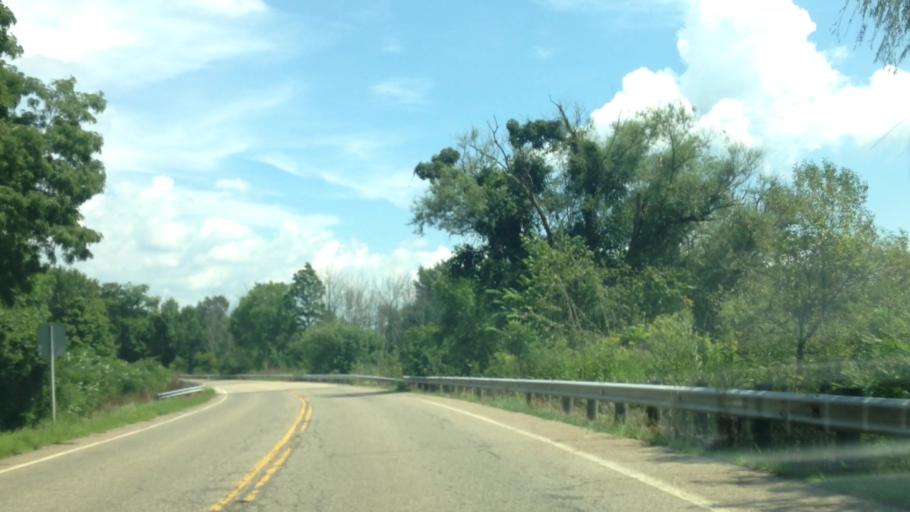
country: US
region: Ohio
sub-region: Summit County
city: Clinton
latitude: 40.9479
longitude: -81.6171
